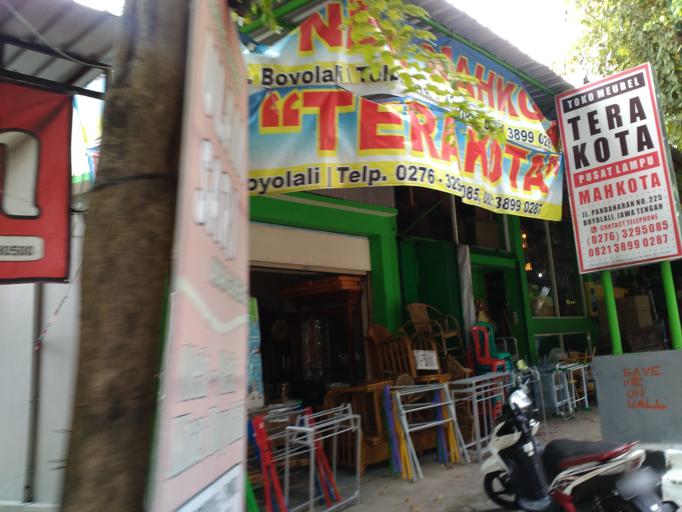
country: ID
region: Central Java
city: Boyolali
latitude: -7.5274
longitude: 110.6011
